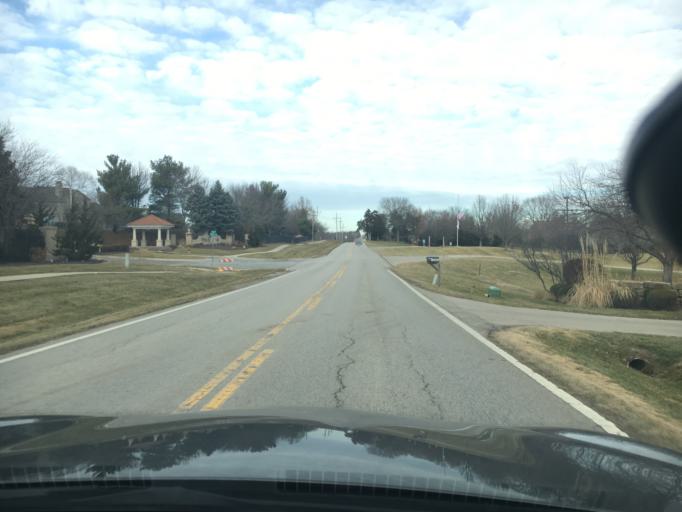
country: US
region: Missouri
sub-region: Jackson County
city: Grandview
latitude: 38.8579
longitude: -94.6305
